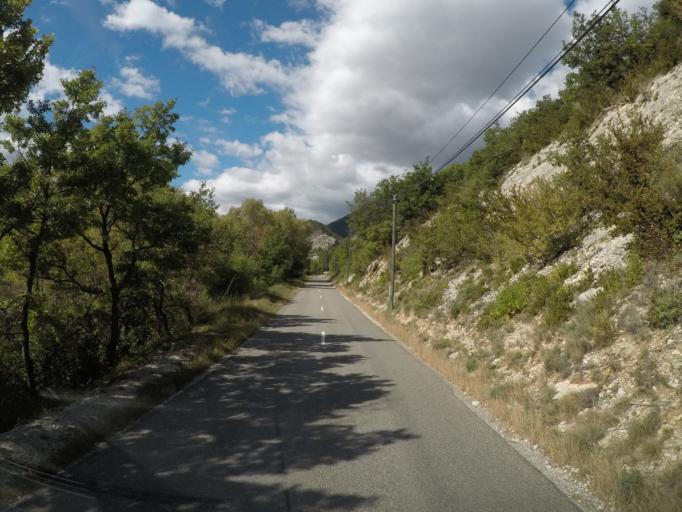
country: FR
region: Provence-Alpes-Cote d'Azur
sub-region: Departement des Hautes-Alpes
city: Laragne-Monteglin
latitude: 44.1747
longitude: 5.7154
